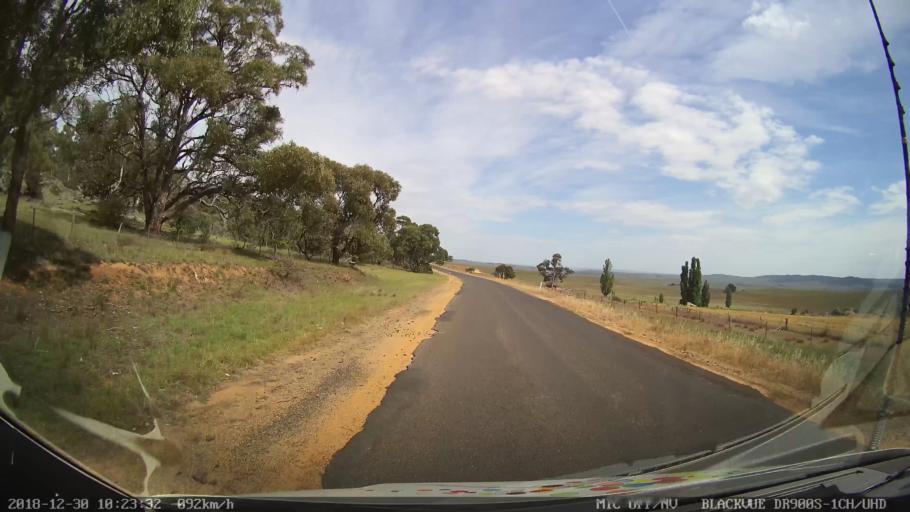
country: AU
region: New South Wales
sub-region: Snowy River
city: Berridale
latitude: -36.5362
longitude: 148.9813
